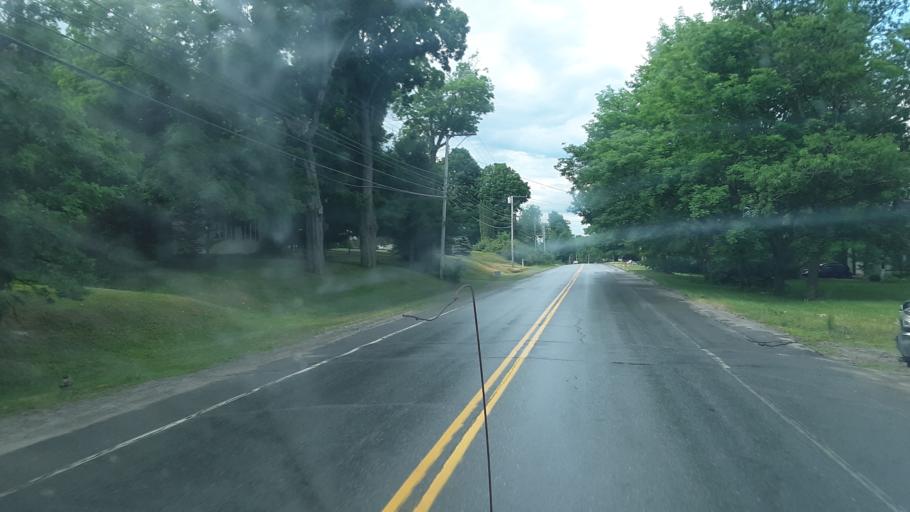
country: US
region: Maine
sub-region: Penobscot County
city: Lincoln
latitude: 45.3806
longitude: -68.4995
